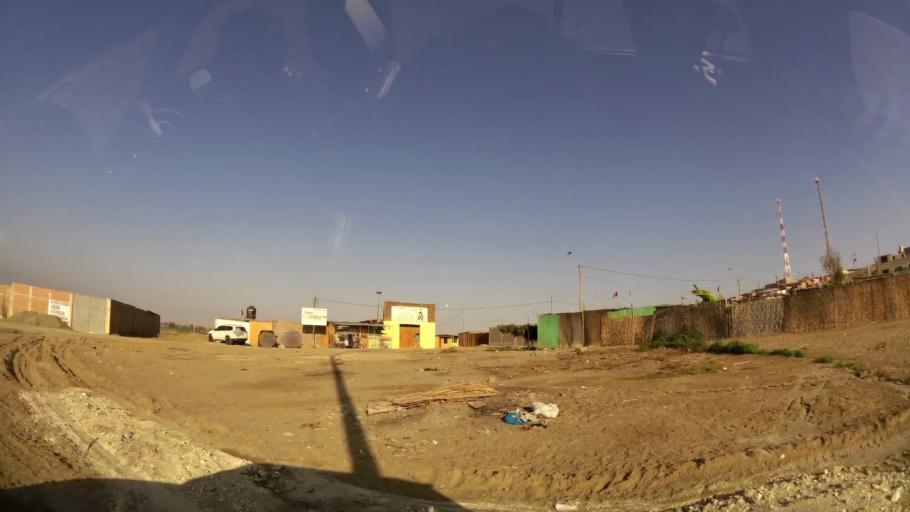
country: PE
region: Ica
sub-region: Provincia de Pisco
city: Villa Tupac Amaru
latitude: -13.7099
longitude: -76.1429
